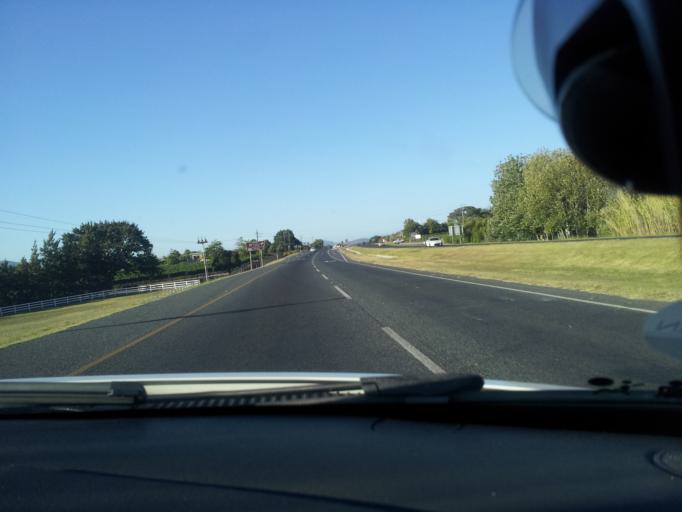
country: ZA
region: Western Cape
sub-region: Cape Winelands District Municipality
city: Stellenbosch
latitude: -34.0163
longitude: 18.8206
